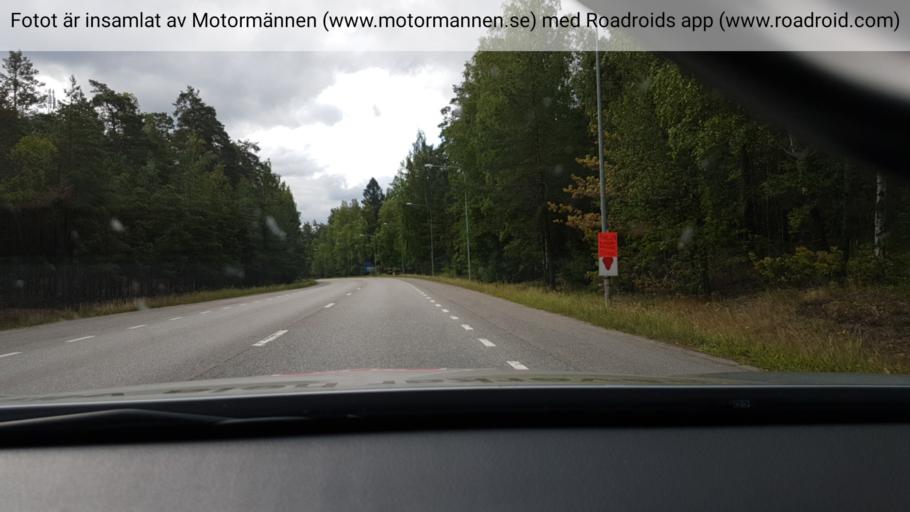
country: SE
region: Stockholm
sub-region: Nacka Kommun
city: Alta
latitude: 59.2363
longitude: 18.1897
